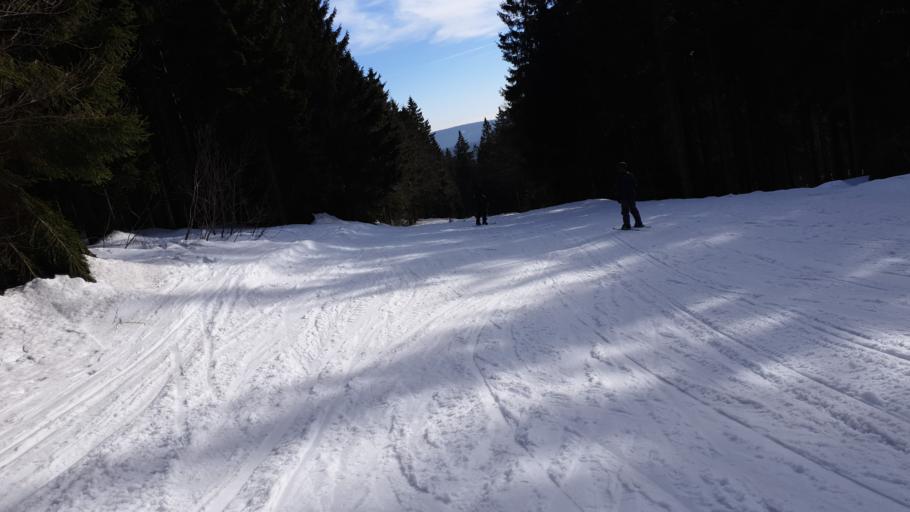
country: DE
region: Bavaria
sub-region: Upper Franconia
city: Bischofsgrun
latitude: 50.0259
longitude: 11.8095
